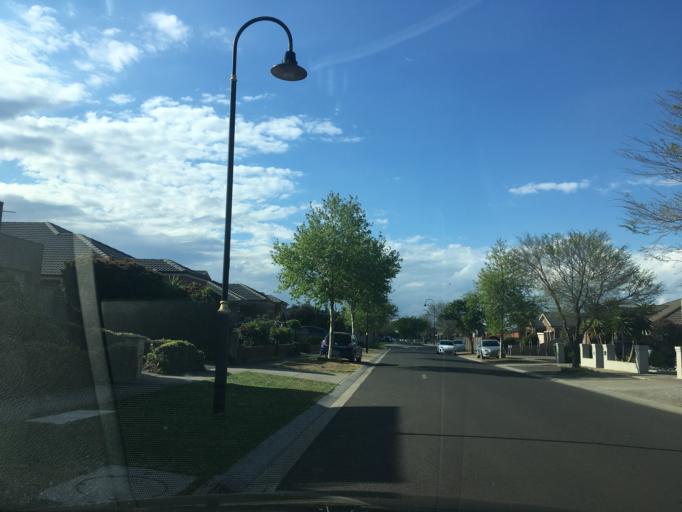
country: AU
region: Victoria
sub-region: Wyndham
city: Hoppers Crossing
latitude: -37.8834
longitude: 144.7267
